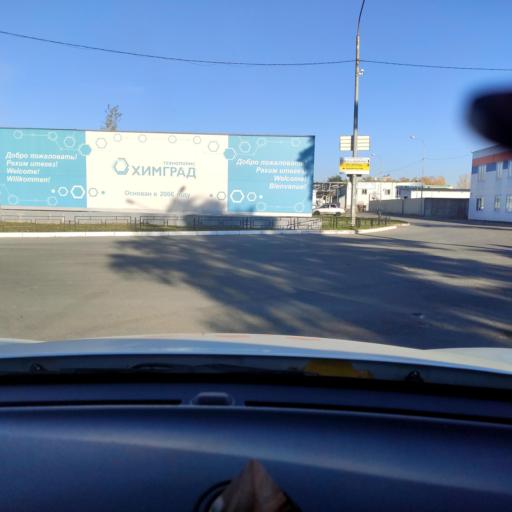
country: RU
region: Tatarstan
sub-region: Gorod Kazan'
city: Kazan
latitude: 55.8345
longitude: 49.0505
